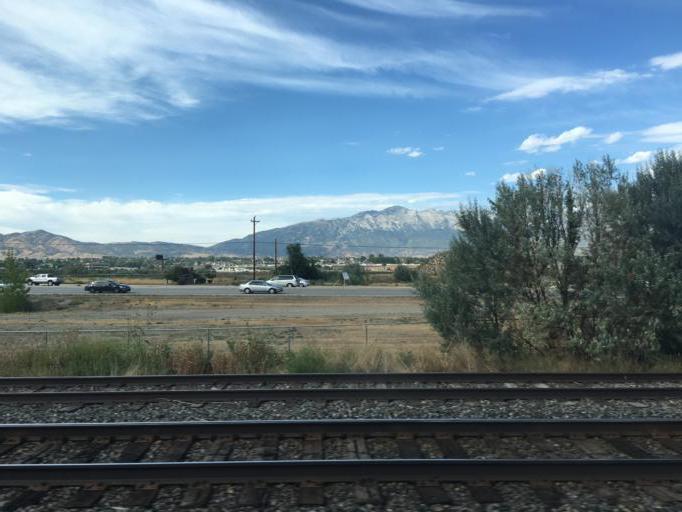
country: US
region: Utah
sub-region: Utah County
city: Lehi
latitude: 40.3766
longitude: -111.8291
